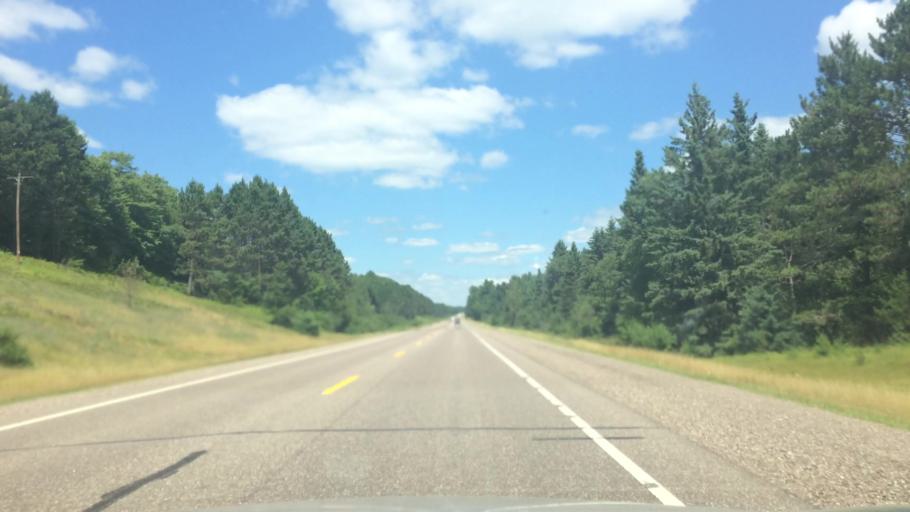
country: US
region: Wisconsin
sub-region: Vilas County
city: Lac du Flambeau
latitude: 45.9554
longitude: -89.7006
